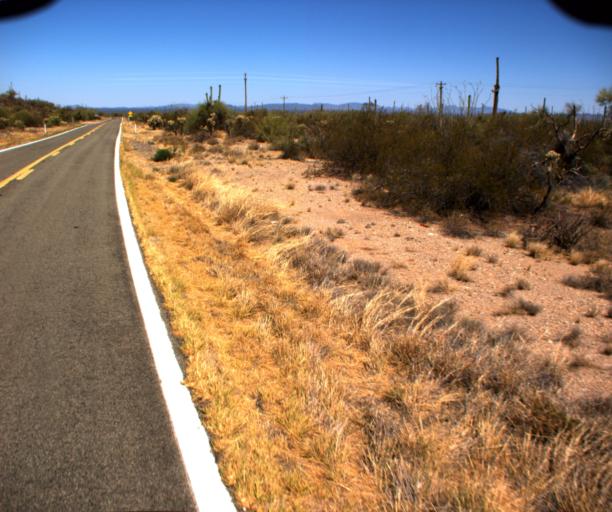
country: US
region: Arizona
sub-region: Pima County
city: Sells
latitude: 32.1761
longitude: -112.2604
